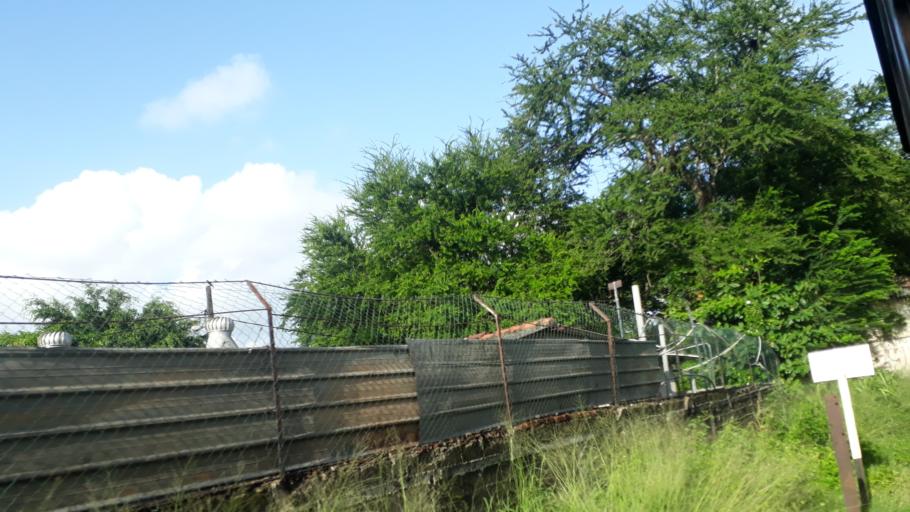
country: LK
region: Western
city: Colombo
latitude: 6.9293
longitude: 79.8579
